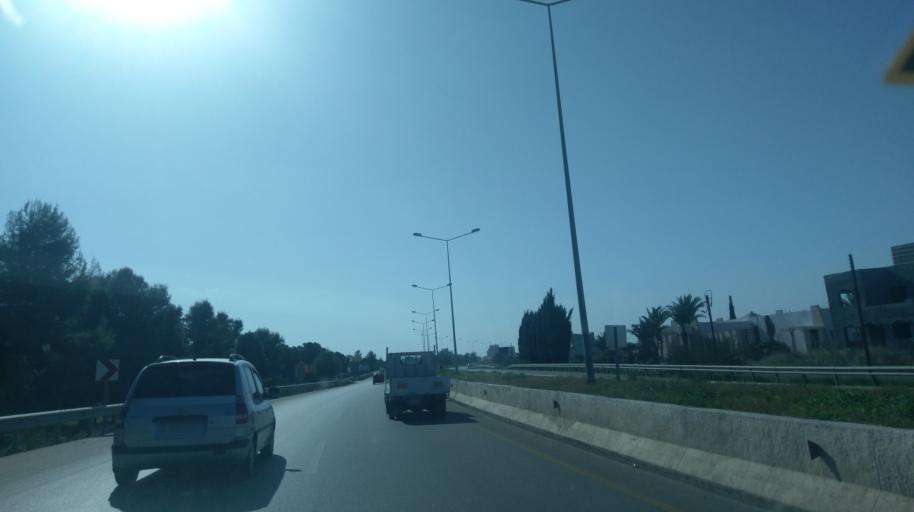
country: CY
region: Ammochostos
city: Trikomo
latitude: 35.2022
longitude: 33.8947
